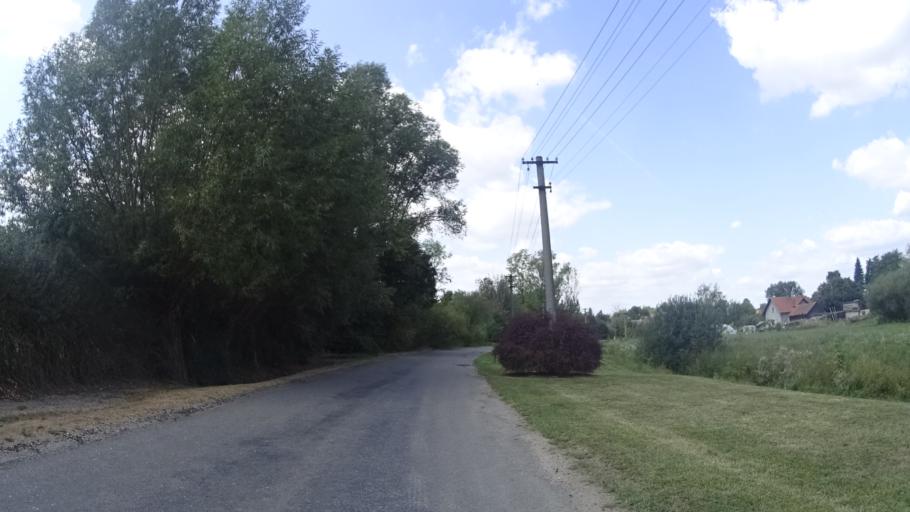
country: CZ
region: Kralovehradecky
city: Kopidlno
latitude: 50.3834
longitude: 15.3013
